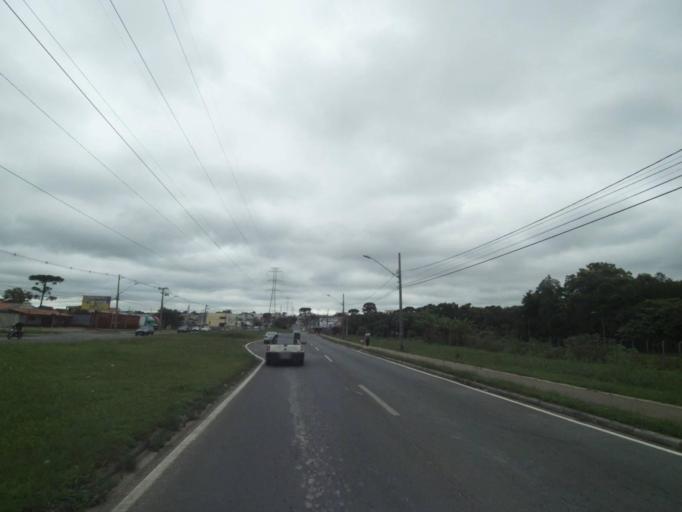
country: BR
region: Parana
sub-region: Araucaria
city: Araucaria
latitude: -25.5559
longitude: -49.3328
